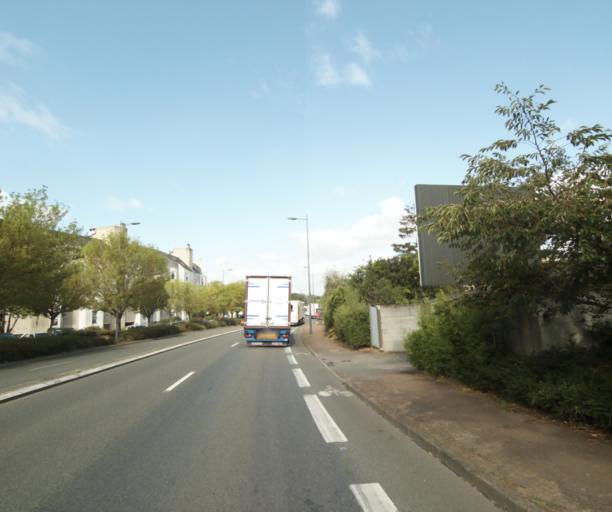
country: FR
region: Pays de la Loire
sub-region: Departement de la Sarthe
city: Sable-sur-Sarthe
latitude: 47.8388
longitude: -0.3240
